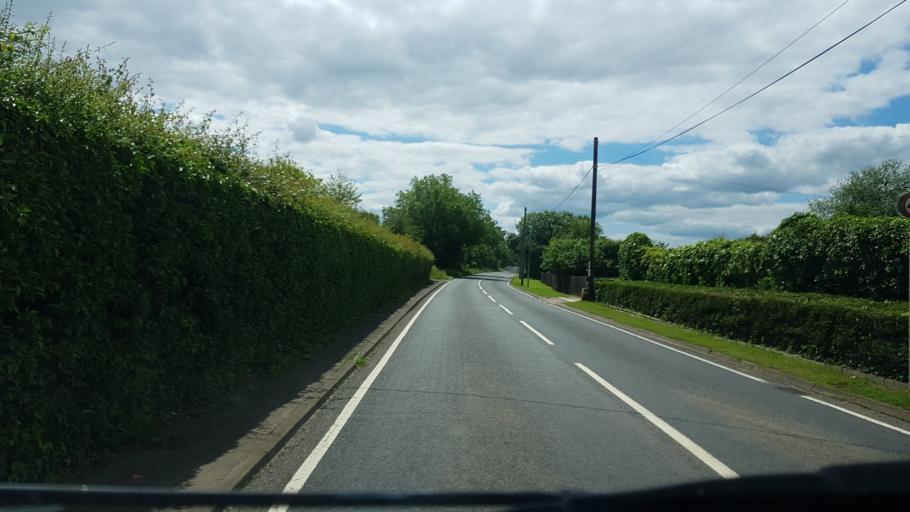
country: GB
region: England
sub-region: Worcestershire
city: Bromsgrove
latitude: 52.2623
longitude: -2.0587
